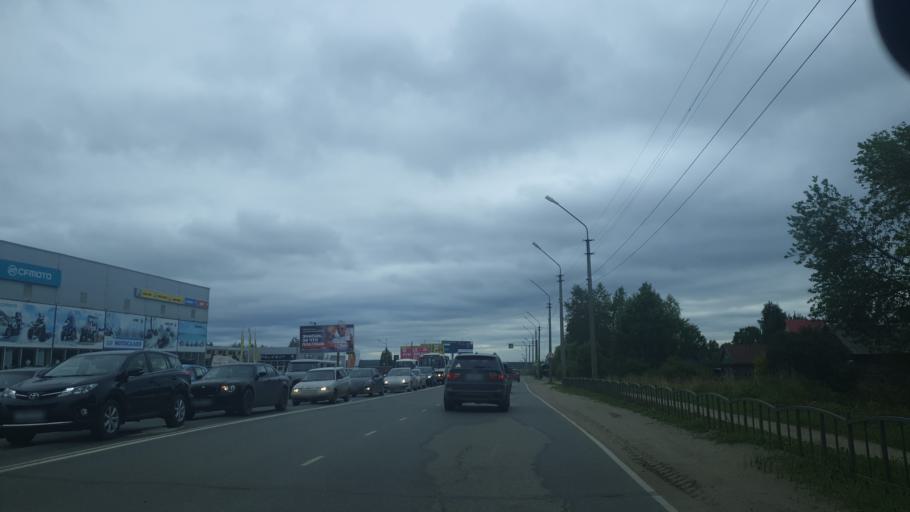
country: RU
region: Komi Republic
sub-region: Syktyvdinskiy Rayon
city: Syktyvkar
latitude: 61.6392
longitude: 50.8149
